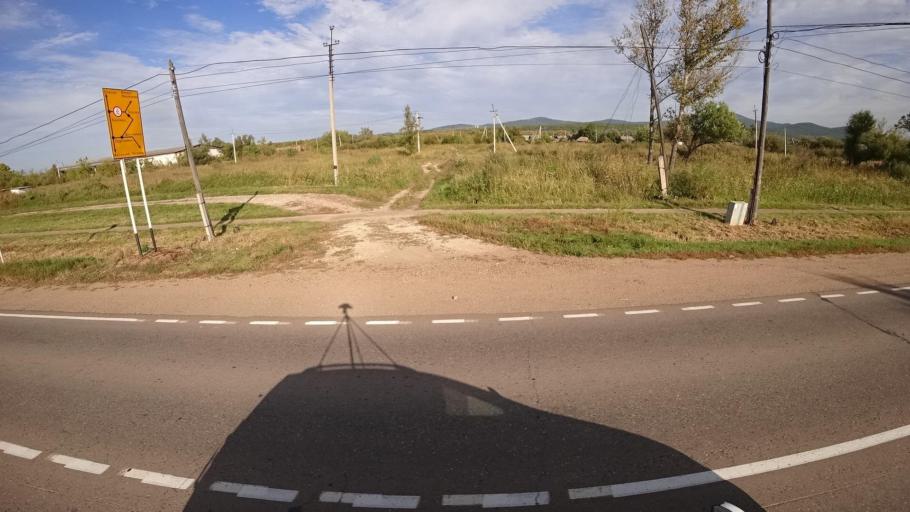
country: RU
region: Primorskiy
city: Dostoyevka
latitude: 44.2918
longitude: 133.4264
